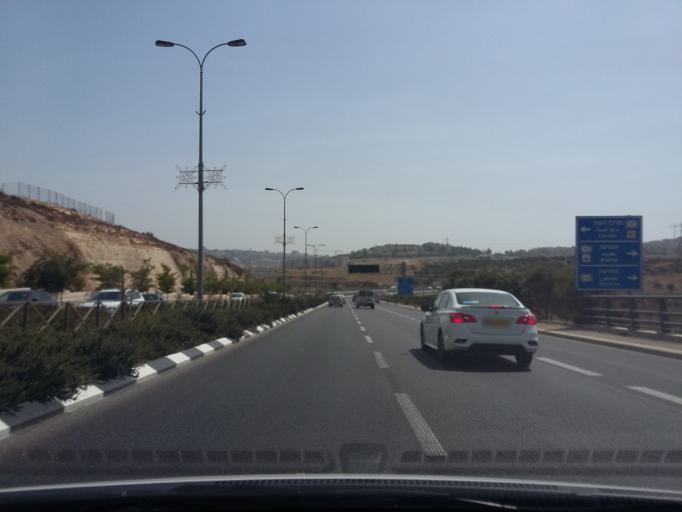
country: PS
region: West Bank
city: Bir Nabala
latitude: 31.8279
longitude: 35.2178
